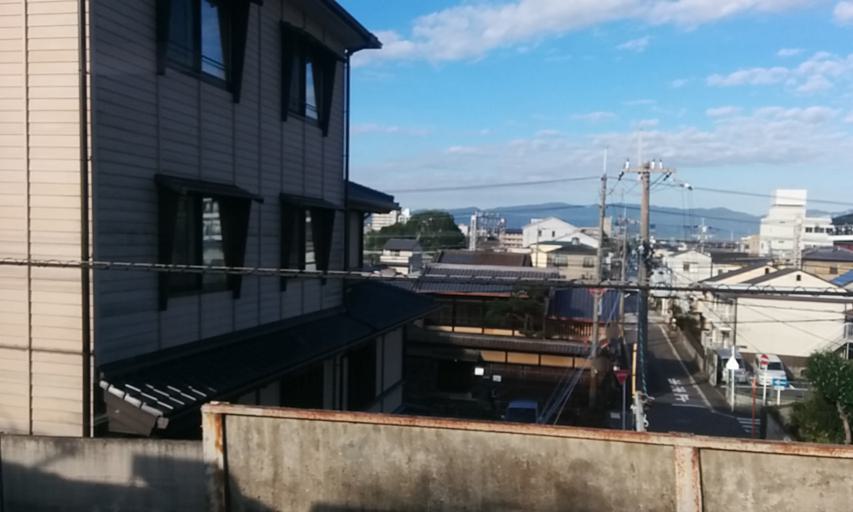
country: JP
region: Kyoto
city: Uji
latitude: 34.9298
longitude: 135.7651
